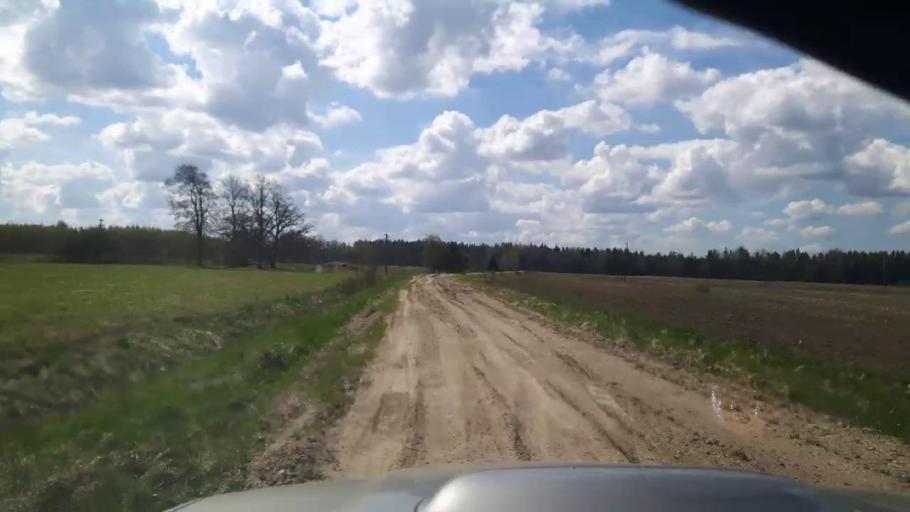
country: EE
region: Paernumaa
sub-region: Vaendra vald (alev)
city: Vandra
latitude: 58.5411
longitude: 25.0694
